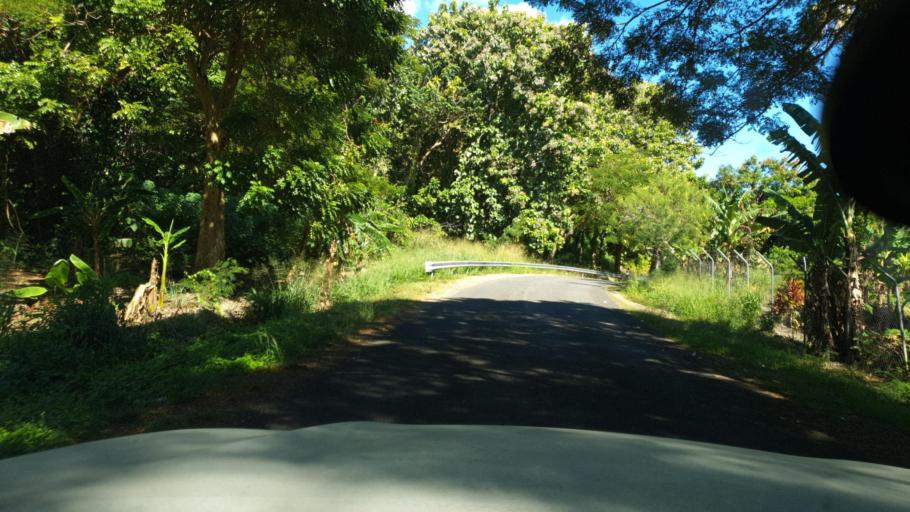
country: SB
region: Guadalcanal
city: Honiara
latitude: -9.2537
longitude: 159.6965
